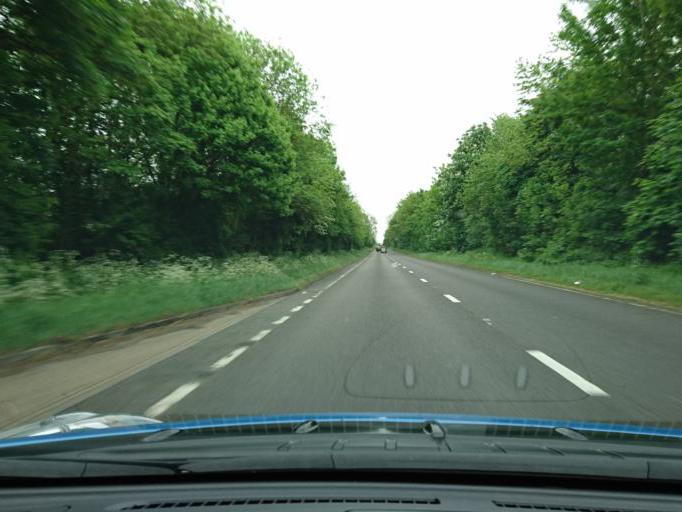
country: GB
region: England
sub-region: Oxfordshire
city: Wheatley
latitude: 51.7613
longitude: -1.1609
